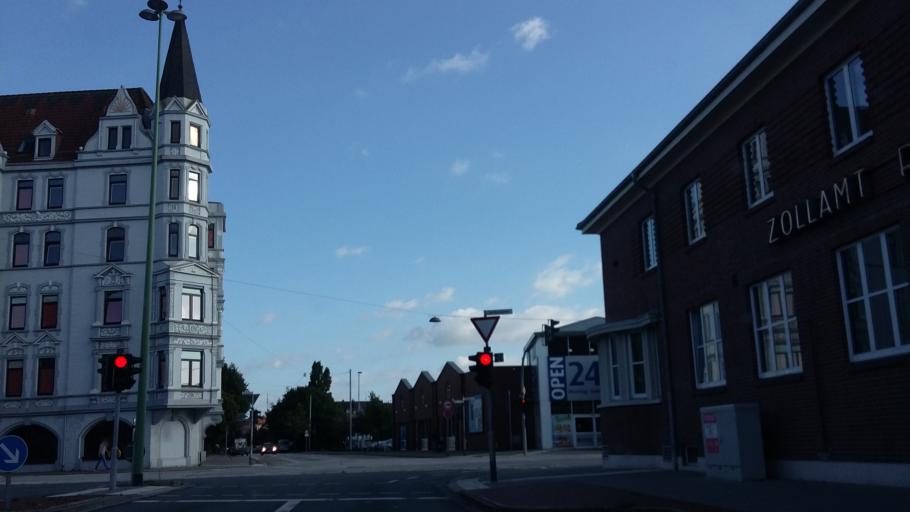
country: DE
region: Bremen
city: Bremerhaven
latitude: 53.5608
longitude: 8.5659
